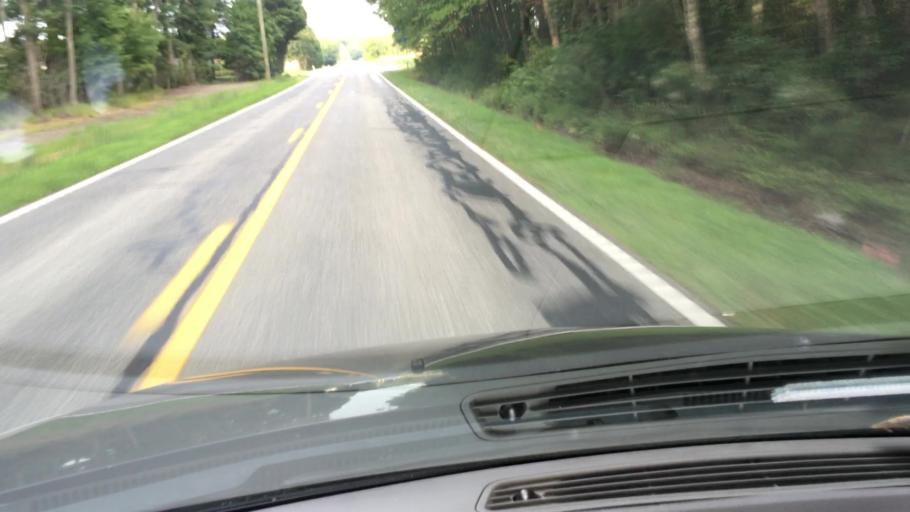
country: US
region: Delaware
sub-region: Sussex County
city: Ocean View
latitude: 38.5174
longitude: -75.0815
